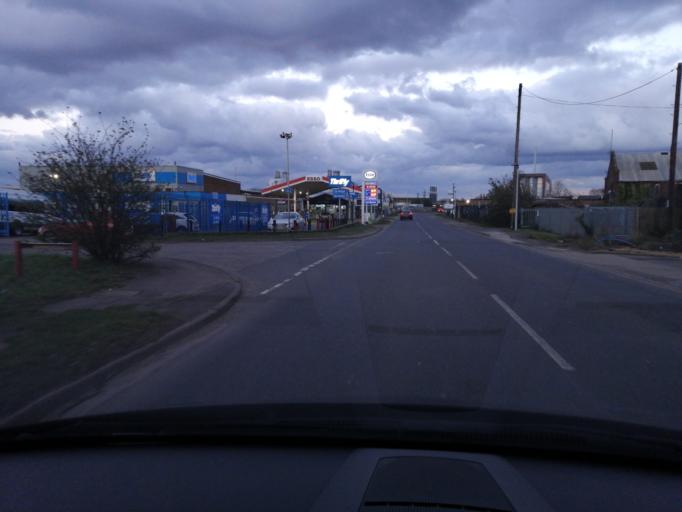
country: GB
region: England
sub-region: Peterborough
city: Peterborough
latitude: 52.5773
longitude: -0.2139
